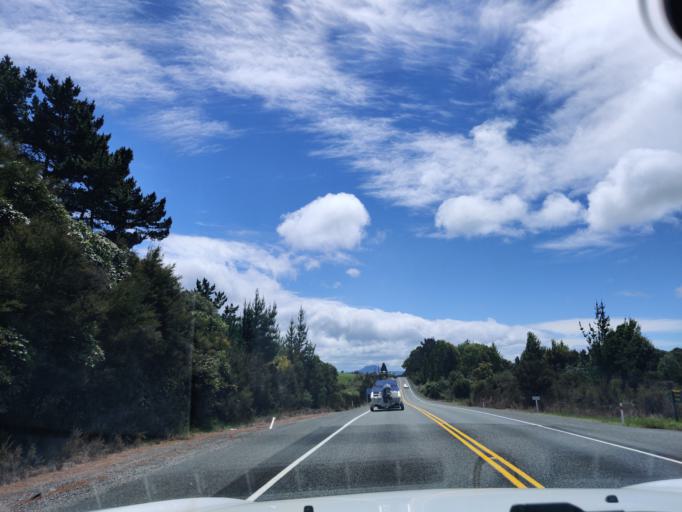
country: NZ
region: Waikato
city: Turangi
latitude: -39.0231
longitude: 175.8094
